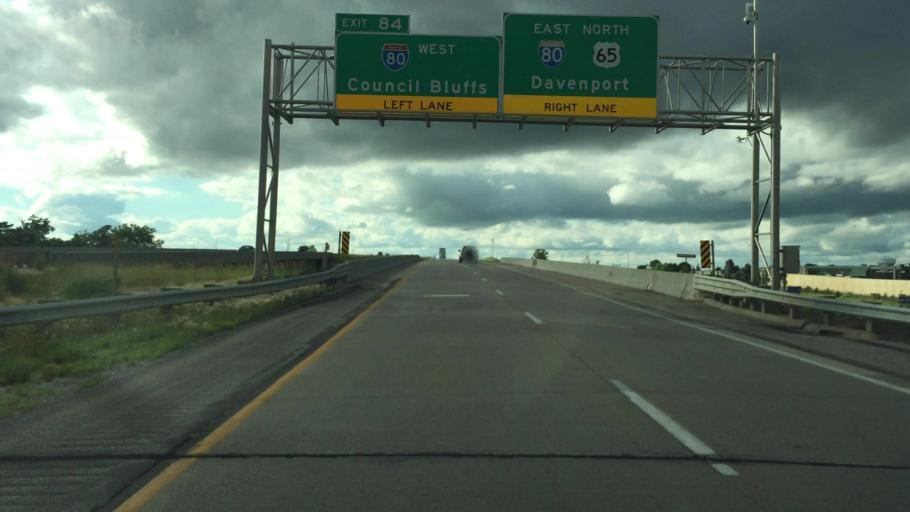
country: US
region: Iowa
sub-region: Polk County
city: Altoona
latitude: 41.6435
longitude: -93.5098
